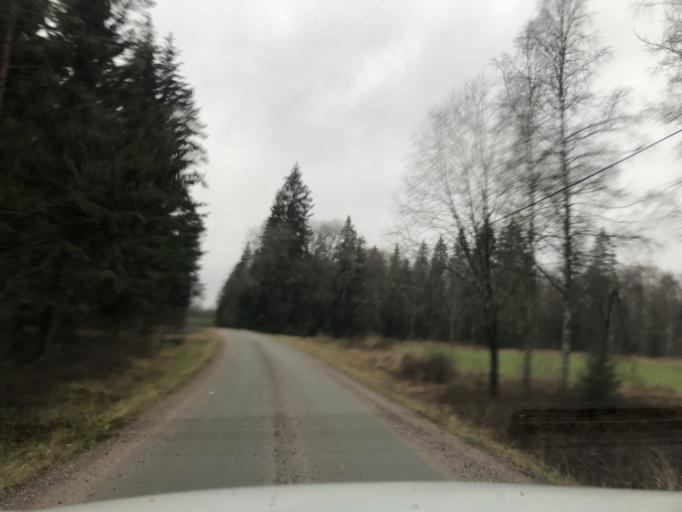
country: SE
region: Vaestra Goetaland
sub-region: Ulricehamns Kommun
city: Ulricehamn
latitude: 57.8615
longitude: 13.6014
